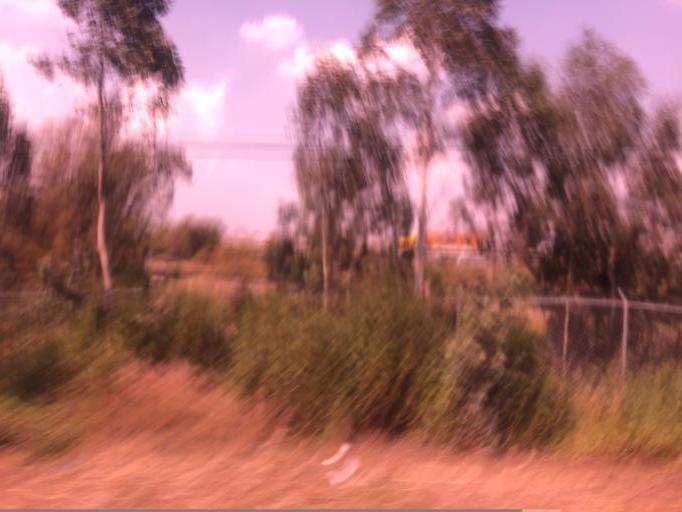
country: MX
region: Mexico
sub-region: Ciudad Nezahualcoyotl
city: Colonia Gustavo Baz Prada
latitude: 19.4683
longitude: -99.0080
